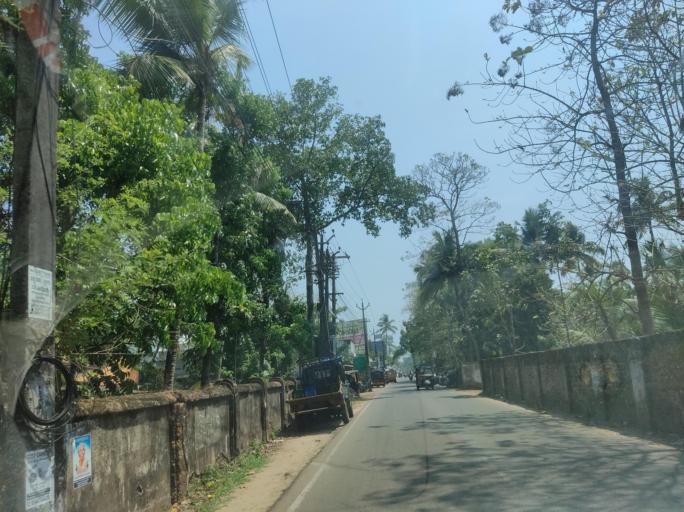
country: IN
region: Kerala
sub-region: Alappuzha
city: Kutiatodu
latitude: 9.8236
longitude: 76.2983
